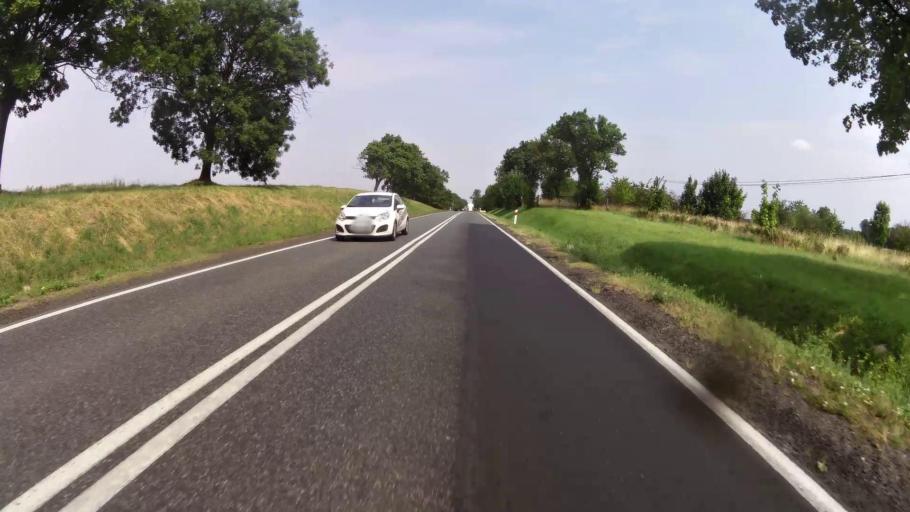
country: PL
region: West Pomeranian Voivodeship
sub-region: Powiat mysliborski
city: Mysliborz
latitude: 52.9403
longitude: 14.9339
